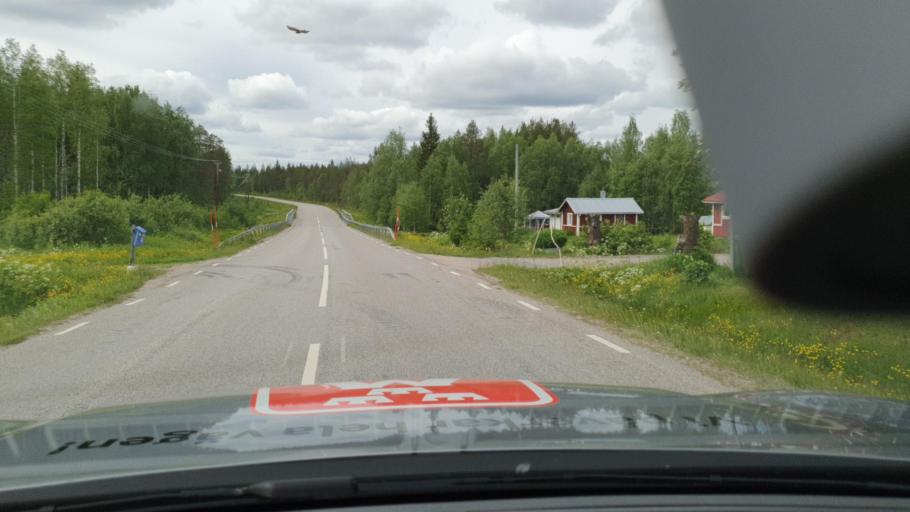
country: FI
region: Lapland
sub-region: Torniolaakso
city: Ylitornio
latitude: 66.0375
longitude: 23.5303
